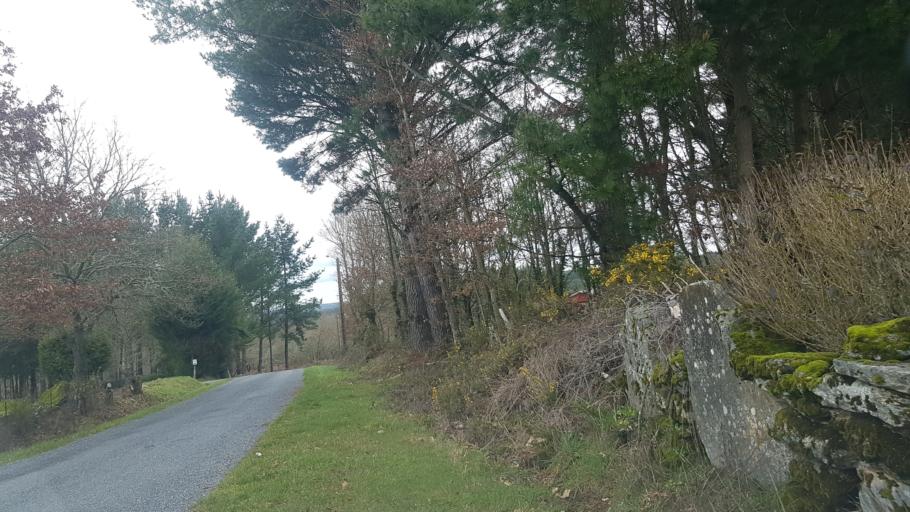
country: ES
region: Galicia
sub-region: Provincia de Lugo
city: Friol
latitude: 43.1164
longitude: -7.8157
